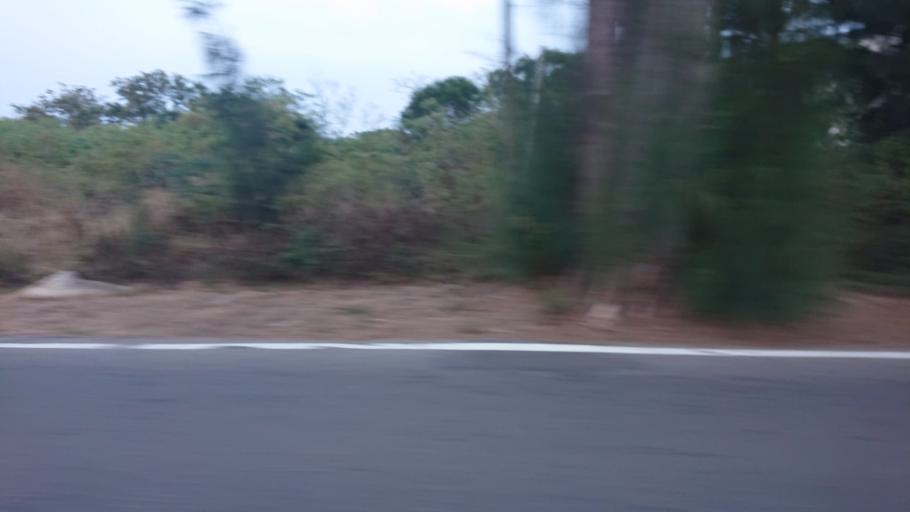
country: TW
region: Fukien
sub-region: Kinmen
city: Jincheng
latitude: 24.4502
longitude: 118.3174
